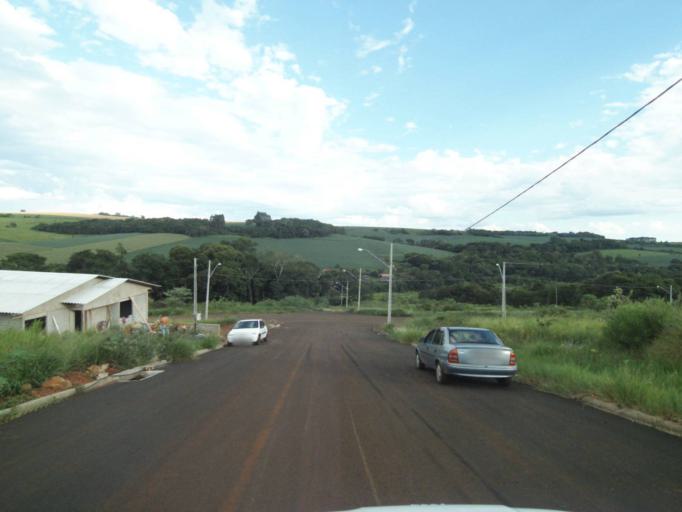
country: BR
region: Parana
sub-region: Laranjeiras Do Sul
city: Laranjeiras do Sul
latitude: -25.4896
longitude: -52.5227
